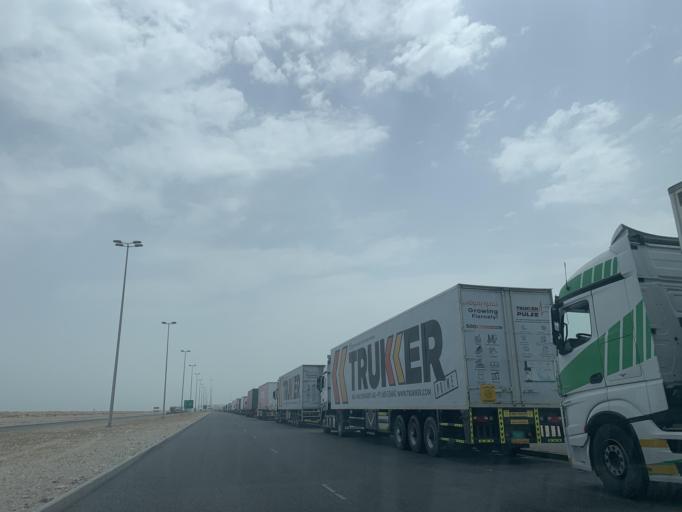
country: BH
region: Muharraq
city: Al Hadd
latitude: 26.2027
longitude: 50.7086
